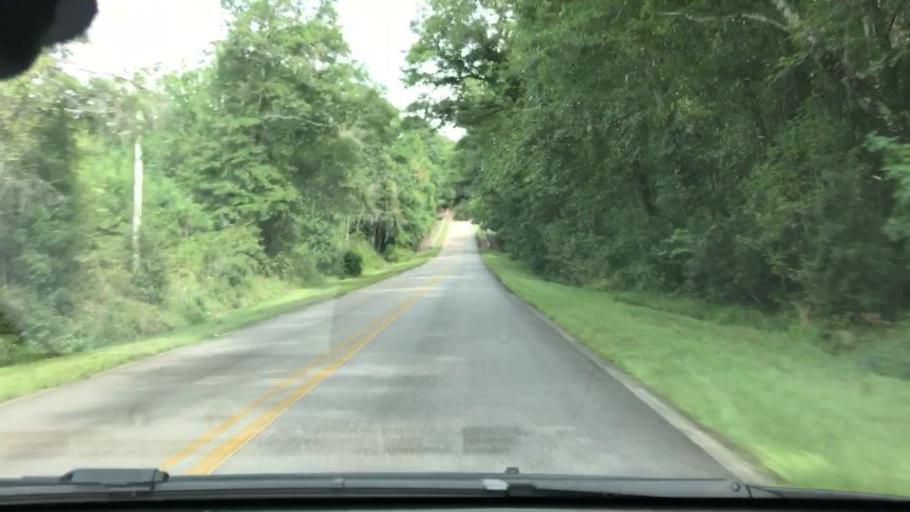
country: US
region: Georgia
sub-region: Clay County
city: Fort Gaines
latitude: 31.5718
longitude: -85.0067
